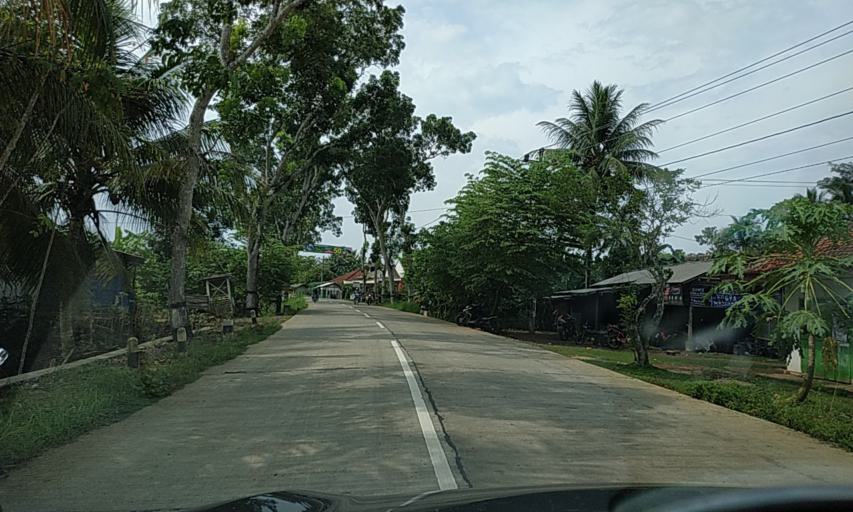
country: ID
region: Central Java
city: Winangun
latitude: -7.3562
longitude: 108.7057
